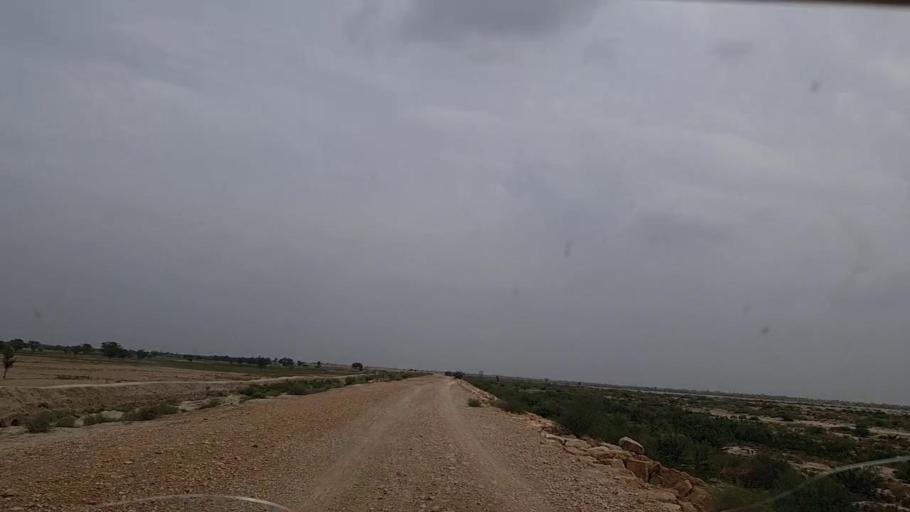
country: PK
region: Sindh
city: Johi
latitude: 26.7145
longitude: 67.5830
